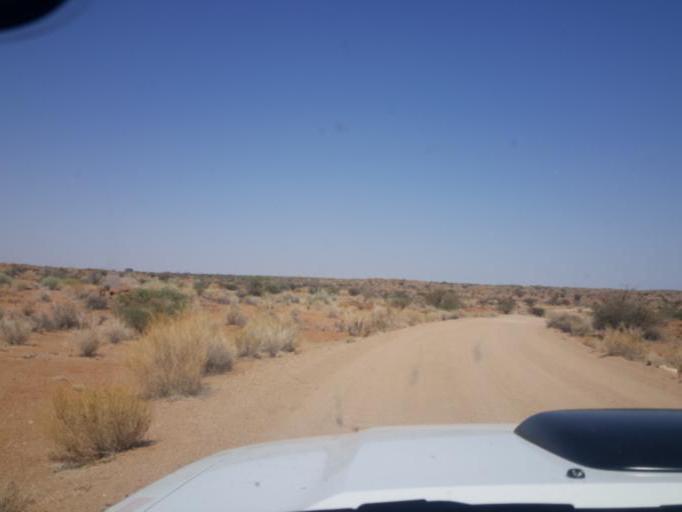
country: ZA
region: Northern Cape
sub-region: Siyanda District Municipality
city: Kakamas
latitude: -28.5972
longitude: 20.2894
